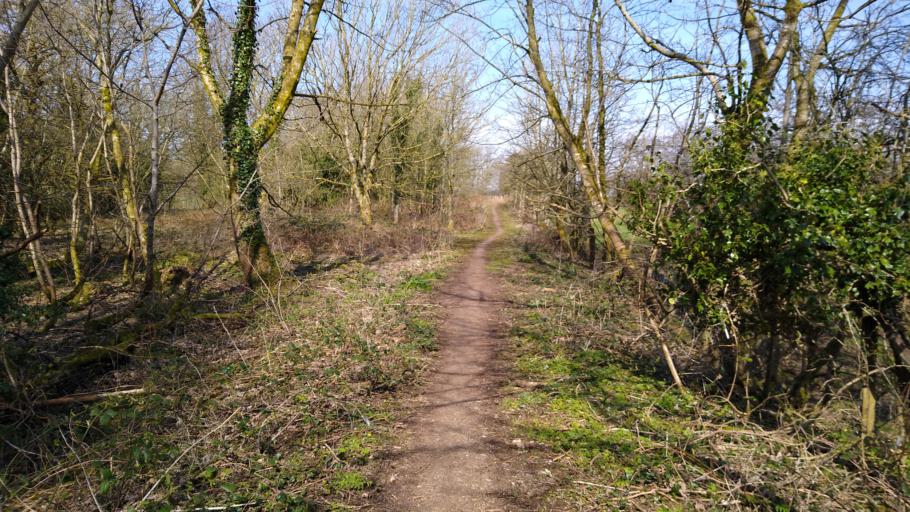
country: GB
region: England
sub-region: Cumbria
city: Dearham
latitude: 54.6736
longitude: -3.4142
